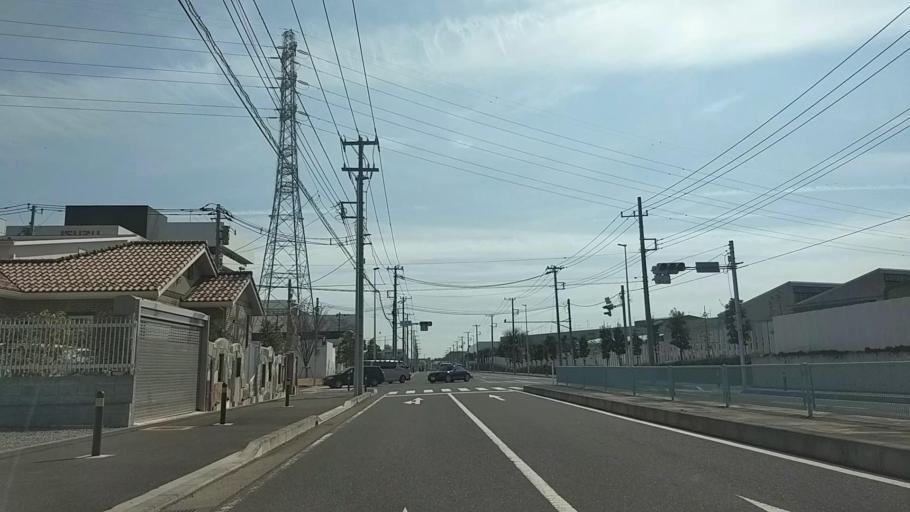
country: JP
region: Kanagawa
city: Fujisawa
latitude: 35.4007
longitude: 139.4558
